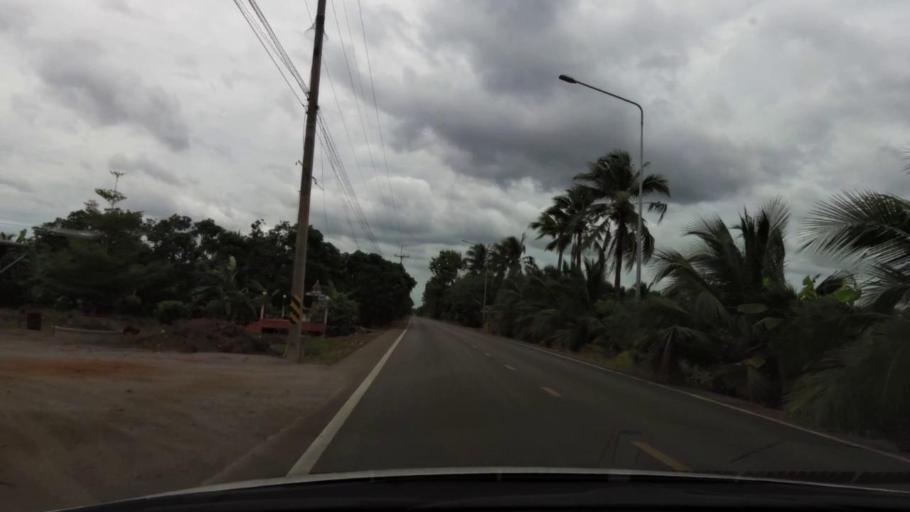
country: TH
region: Ratchaburi
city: Damnoen Saduak
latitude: 13.5562
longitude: 100.0153
